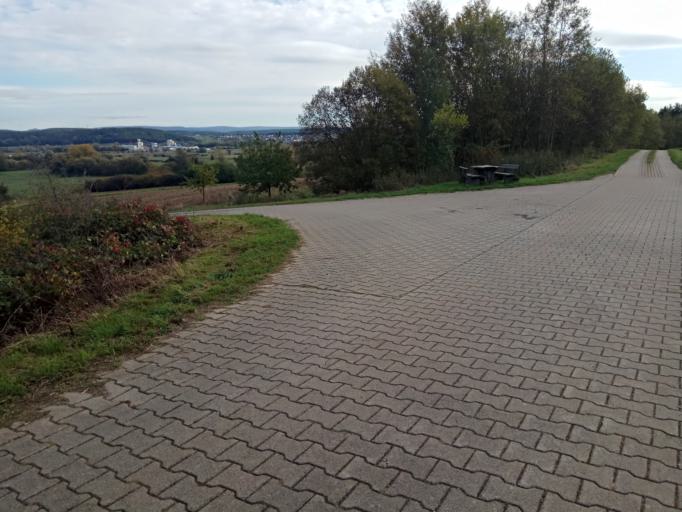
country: DE
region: Bavaria
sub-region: Upper Franconia
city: Baunach
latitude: 49.9978
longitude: 10.8639
